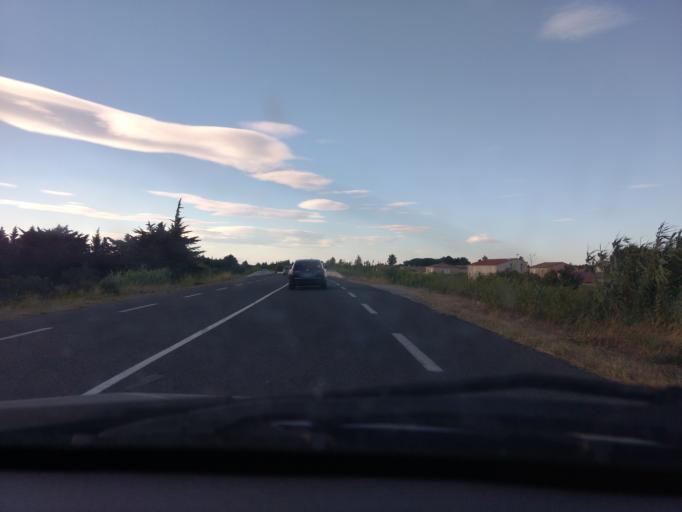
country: FR
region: Languedoc-Roussillon
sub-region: Departement des Pyrenees-Orientales
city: Sainte-Marie-Plage
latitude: 42.7223
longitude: 3.0299
